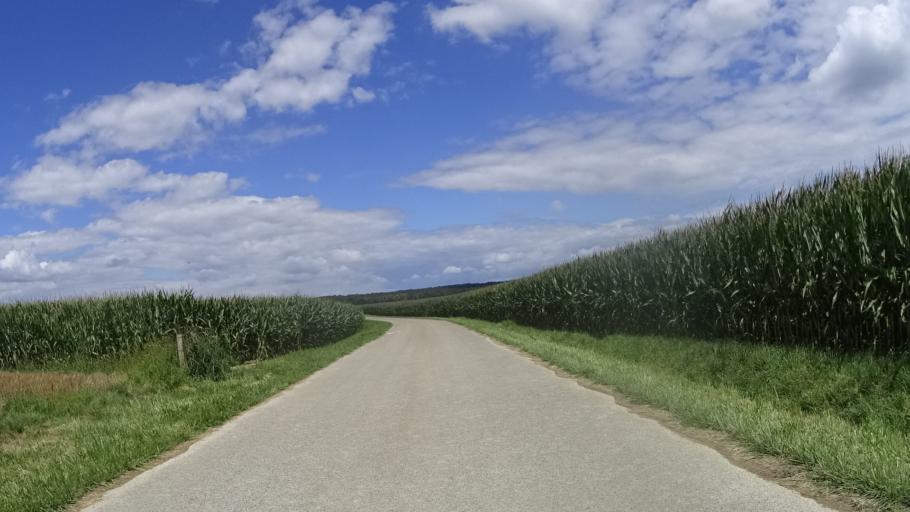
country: FR
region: Champagne-Ardenne
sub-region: Departement de la Haute-Marne
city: Montier-en-Der
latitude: 48.5126
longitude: 4.7747
